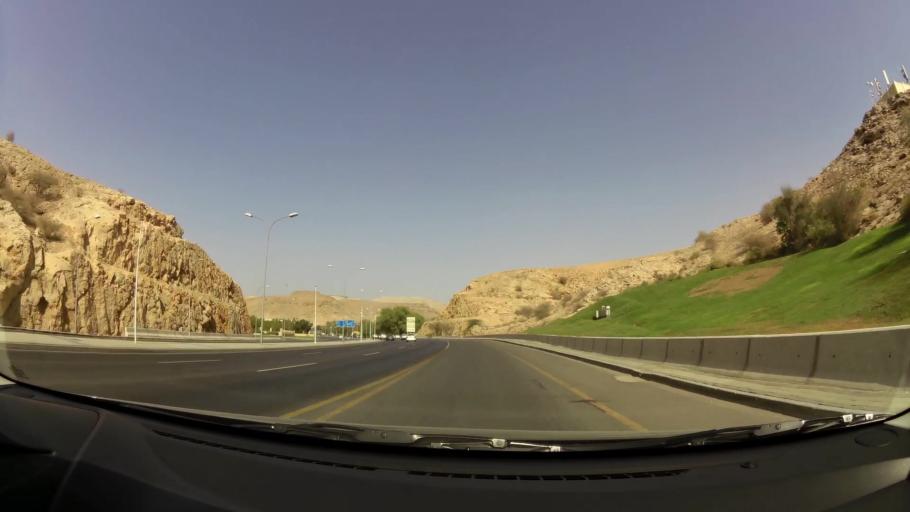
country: OM
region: Muhafazat Masqat
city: Muscat
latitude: 23.6071
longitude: 58.5030
